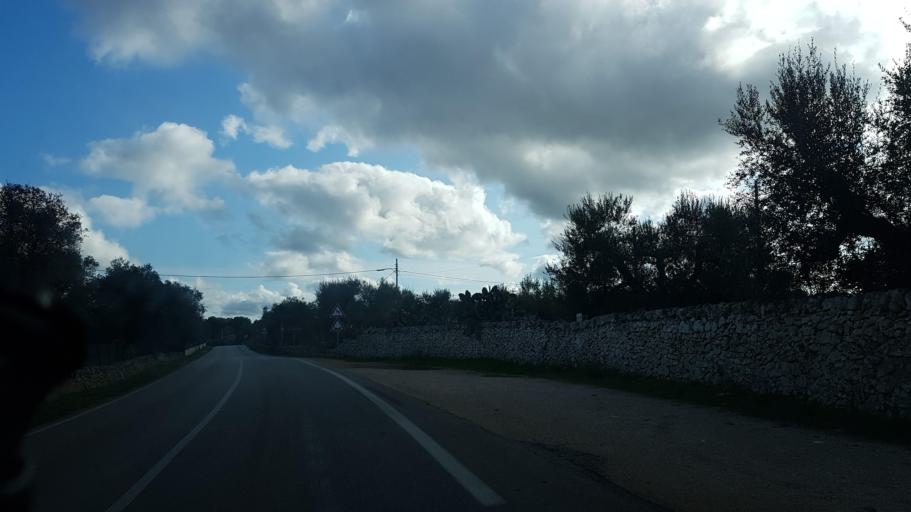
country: IT
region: Apulia
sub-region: Provincia di Brindisi
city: Ostuni
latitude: 40.6759
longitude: 17.5932
